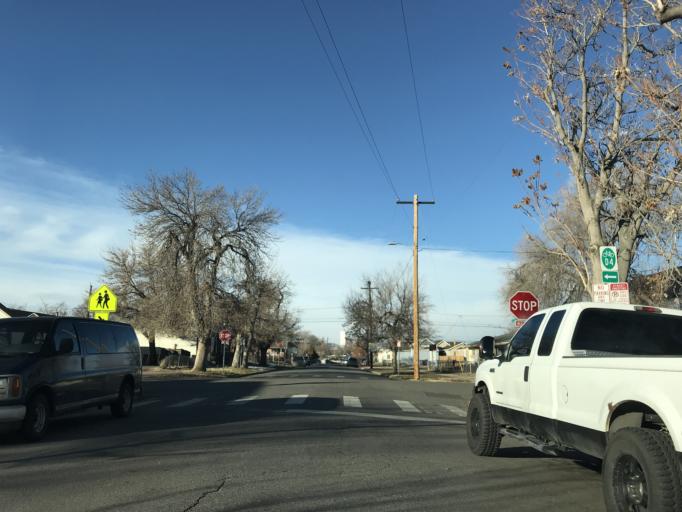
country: US
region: Colorado
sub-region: Denver County
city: Denver
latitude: 39.7658
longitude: -104.9704
